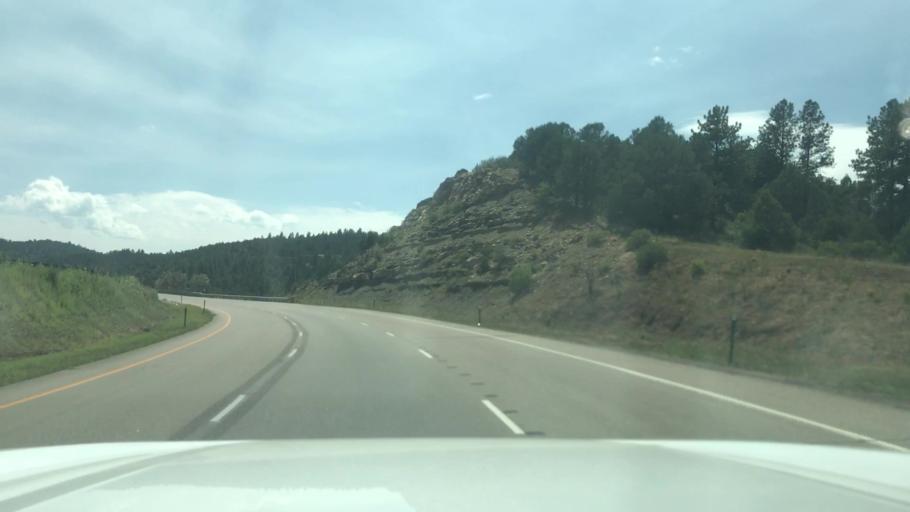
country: US
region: Colorado
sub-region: Las Animas County
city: Trinidad
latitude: 37.0618
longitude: -104.5228
